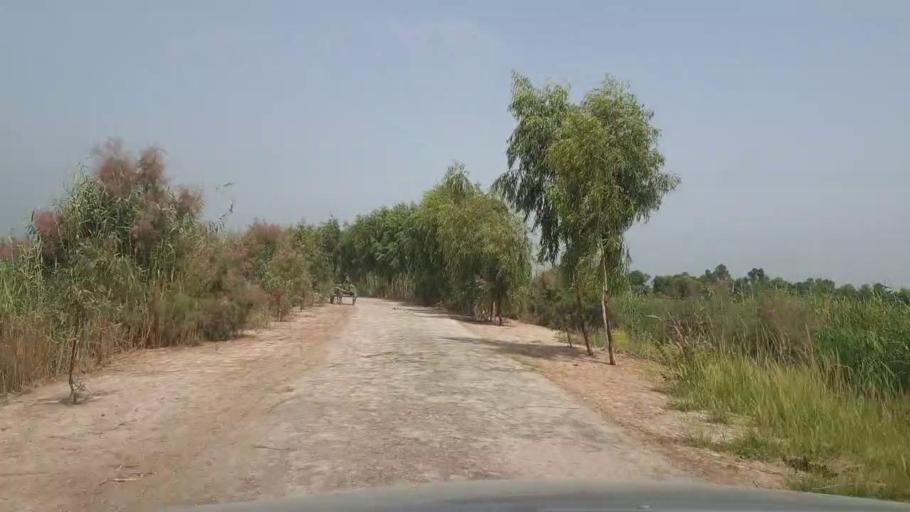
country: PK
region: Sindh
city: Garhi Yasin
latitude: 27.9463
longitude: 68.3721
